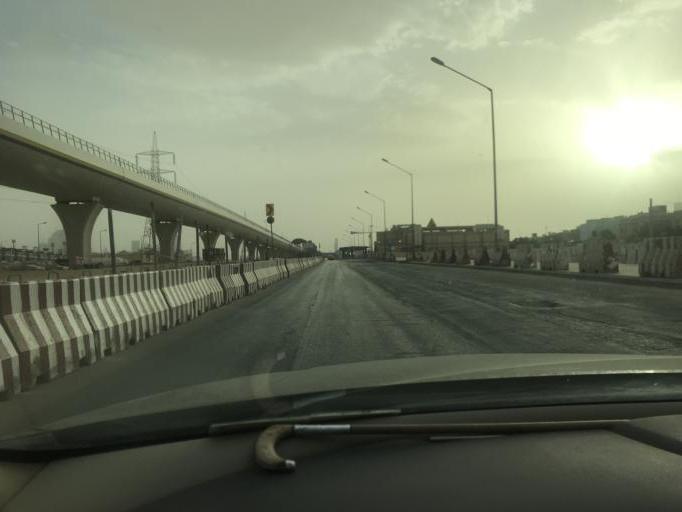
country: SA
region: Ar Riyad
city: Riyadh
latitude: 24.7888
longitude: 46.6652
